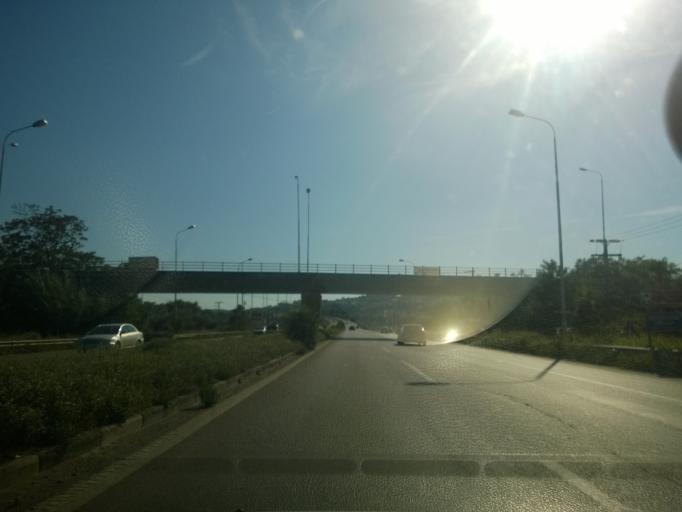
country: GR
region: Central Macedonia
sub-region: Nomos Thessalonikis
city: Neo Rysi
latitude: 40.4969
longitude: 23.0023
